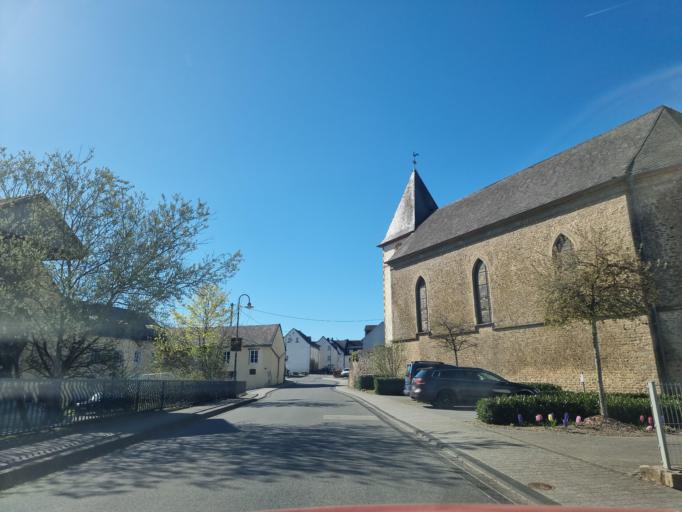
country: DE
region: Rheinland-Pfalz
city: Niederweis
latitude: 49.8722
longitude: 6.4657
